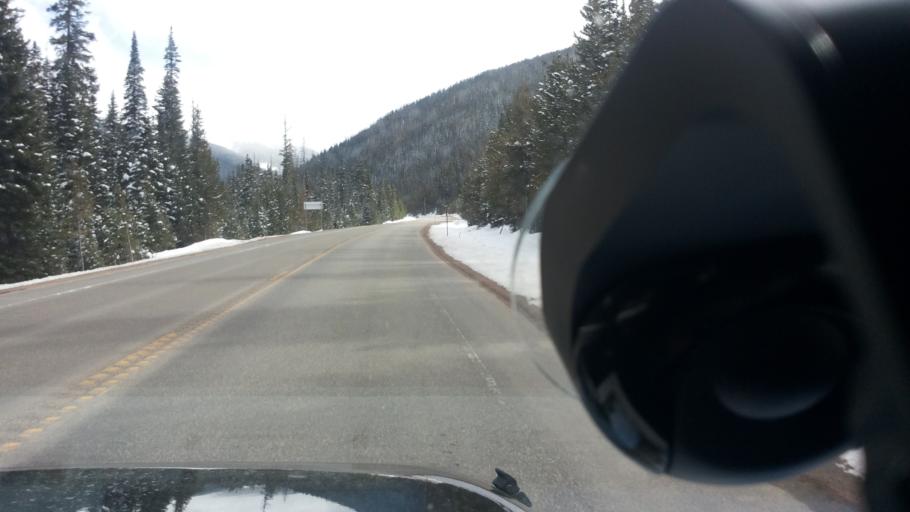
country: US
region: Colorado
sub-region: Grand County
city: Fraser
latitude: 39.8612
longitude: -105.7507
